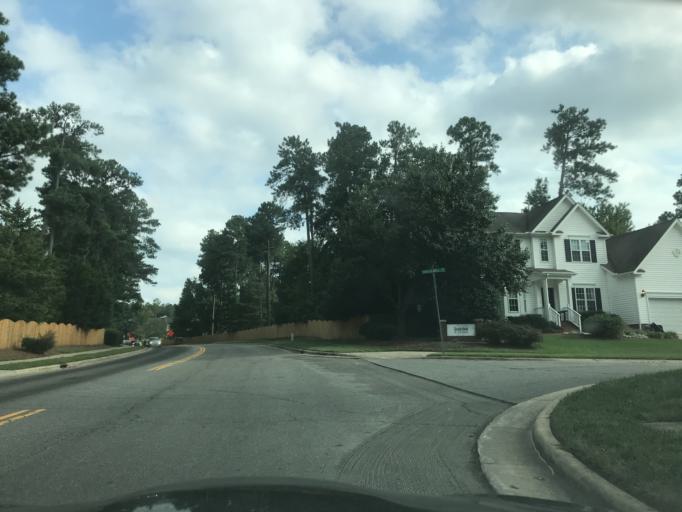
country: US
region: North Carolina
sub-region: Durham County
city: Durham
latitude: 35.9046
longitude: -78.9319
